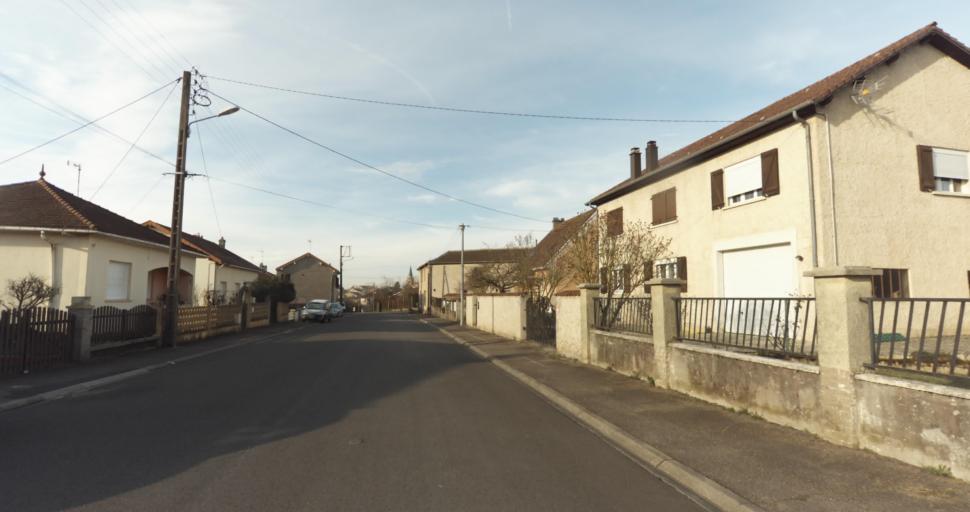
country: FR
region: Lorraine
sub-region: Departement de Meurthe-et-Moselle
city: Jarny
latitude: 49.1591
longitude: 5.8914
